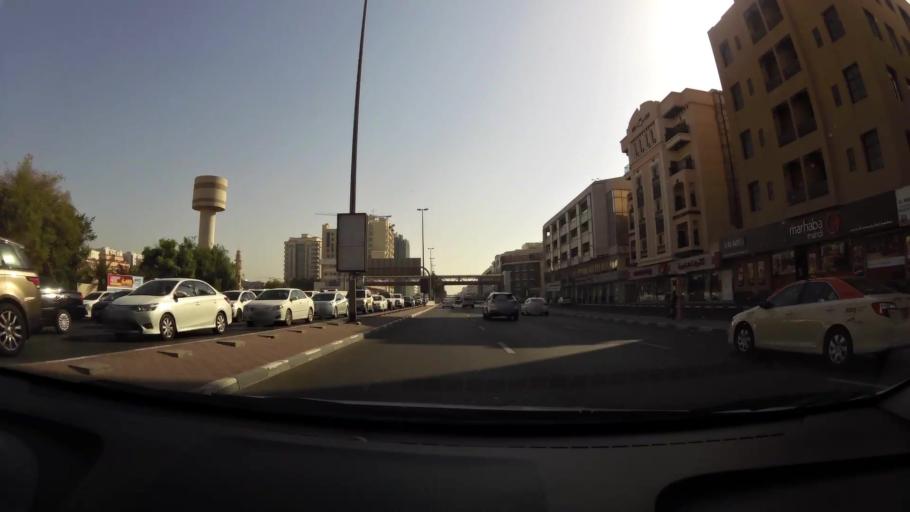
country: AE
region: Ash Shariqah
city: Sharjah
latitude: 25.2694
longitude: 55.3791
